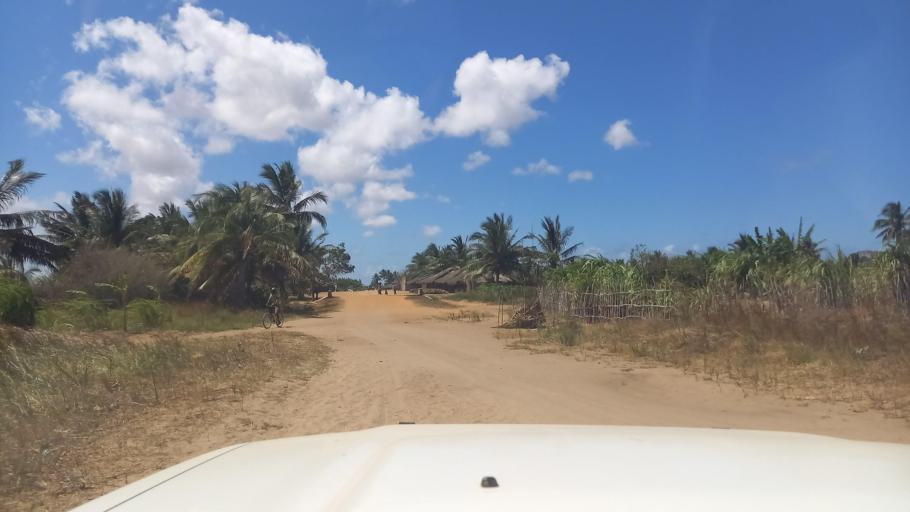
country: MZ
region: Cabo Delgado
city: Pemba
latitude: -13.4198
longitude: 40.5193
